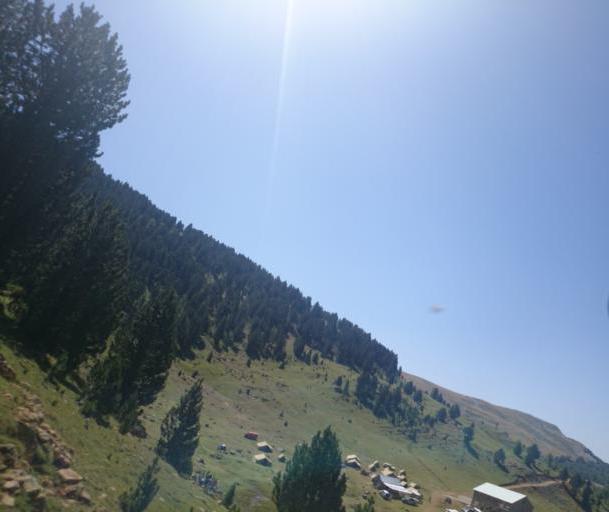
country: AL
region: Korce
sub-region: Rrethi i Korces
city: Moglice
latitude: 40.7606
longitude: 20.4350
